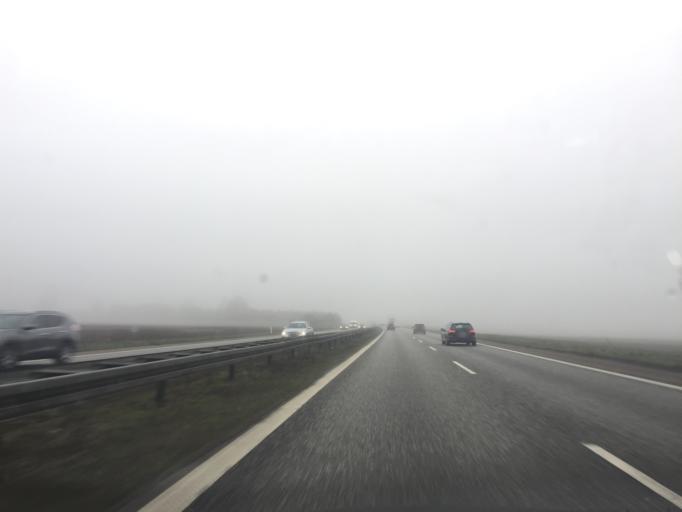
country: DK
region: Zealand
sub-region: Ringsted Kommune
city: Ringsted
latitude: 55.4489
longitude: 11.6920
